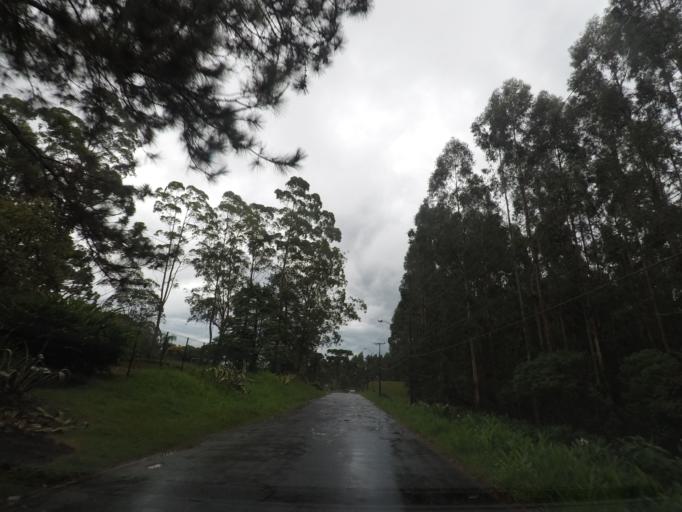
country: BR
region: Parana
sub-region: Campo Largo
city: Campo Largo
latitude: -25.4557
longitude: -49.4364
